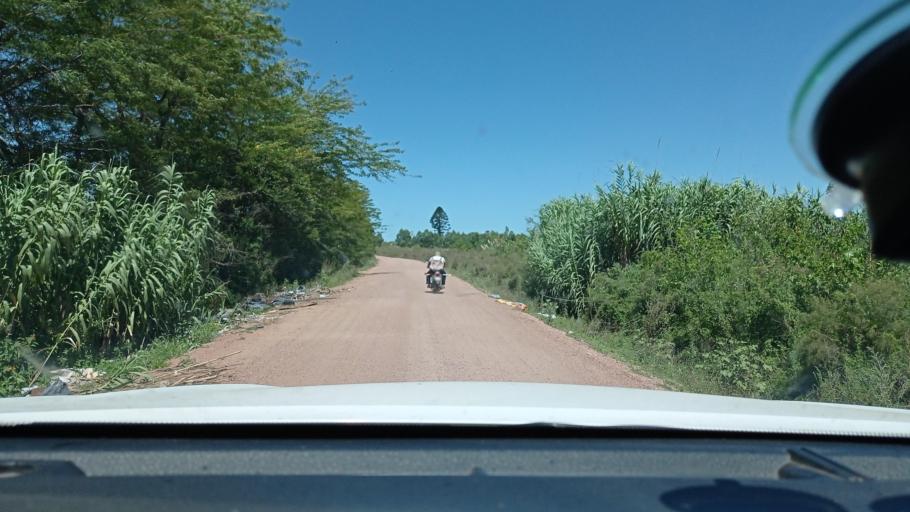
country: UY
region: Canelones
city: Las Piedras
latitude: -34.7426
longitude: -56.2110
